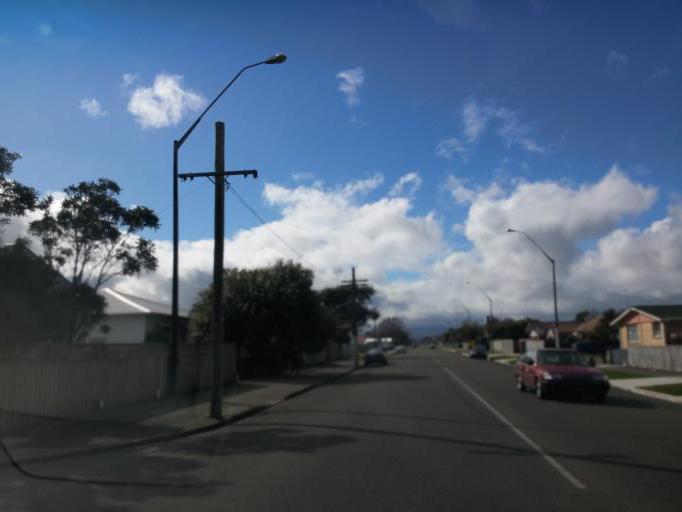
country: NZ
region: Manawatu-Wanganui
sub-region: Palmerston North City
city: Palmerston North
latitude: -40.3625
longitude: 175.6066
